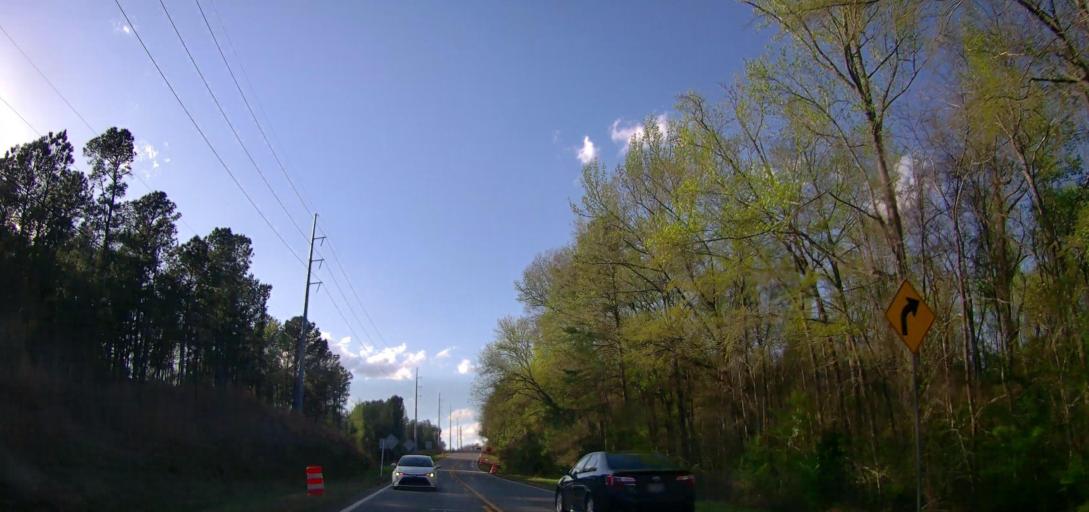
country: US
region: Georgia
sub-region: Baldwin County
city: Milledgeville
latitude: 33.1019
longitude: -83.2736
